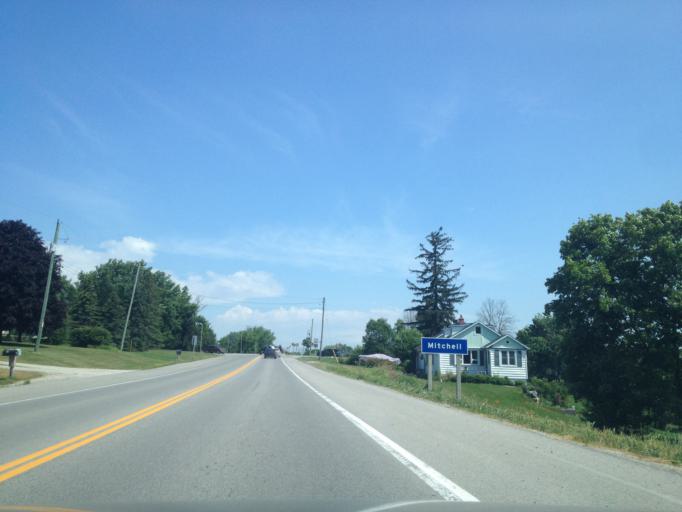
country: CA
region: Ontario
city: Huron East
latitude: 43.4593
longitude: -81.2056
